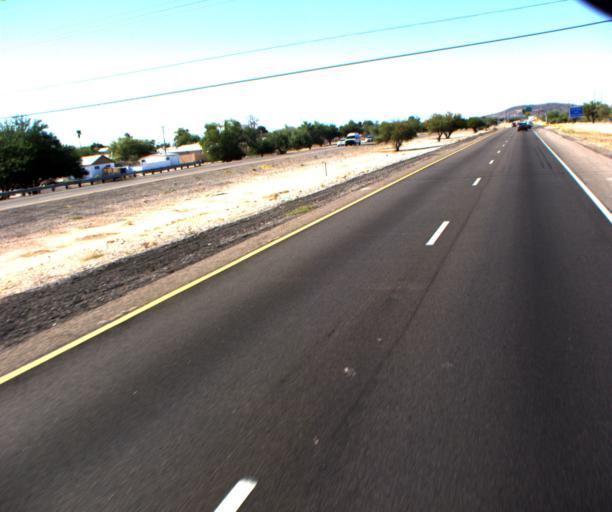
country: US
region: Arizona
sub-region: Pima County
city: Drexel Heights
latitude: 32.1482
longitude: -110.9868
